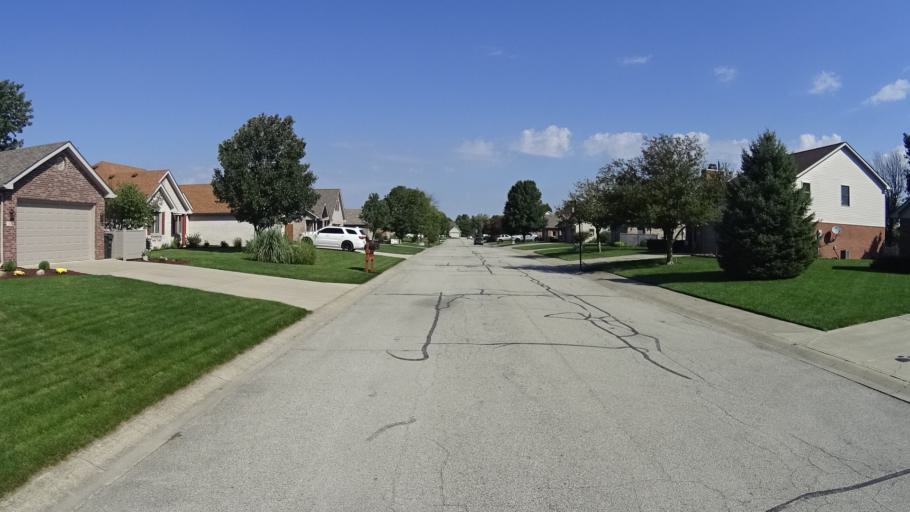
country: US
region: Indiana
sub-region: Madison County
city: Lapel
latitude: 40.0572
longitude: -85.8492
